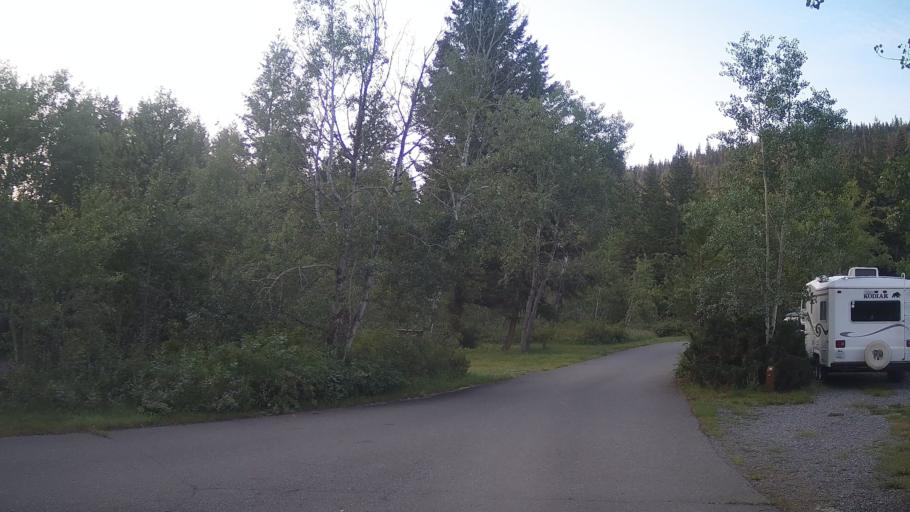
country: CA
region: British Columbia
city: Hanceville
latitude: 52.0887
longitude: -123.3963
